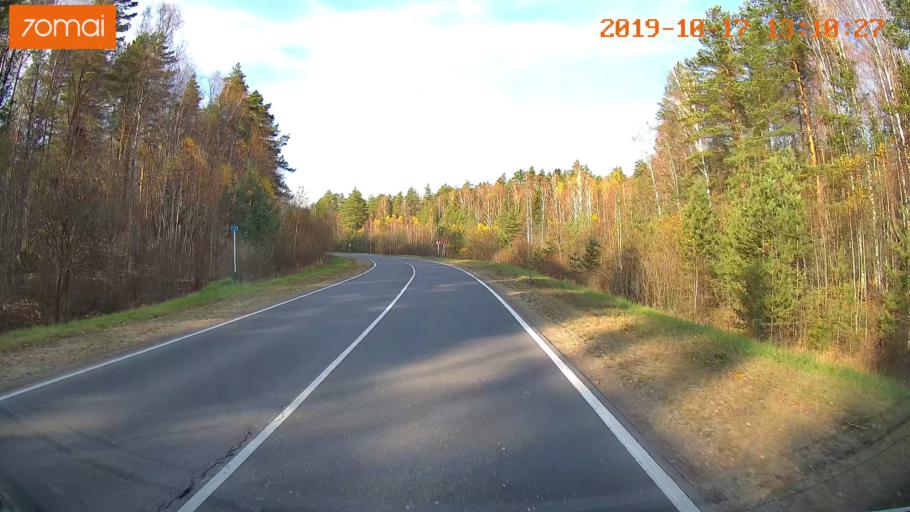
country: RU
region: Rjazan
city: Syntul
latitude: 55.0189
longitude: 41.2563
